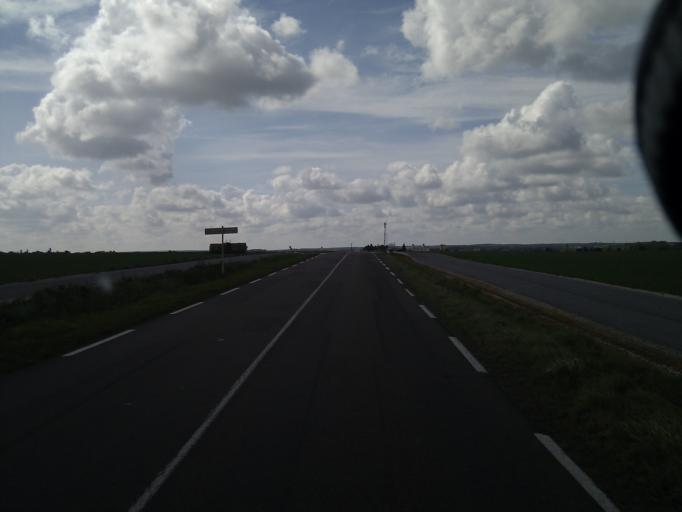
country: FR
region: Bourgogne
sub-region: Departement de la Cote-d'Or
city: Chatillon-sur-Seine
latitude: 47.8789
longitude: 4.5898
